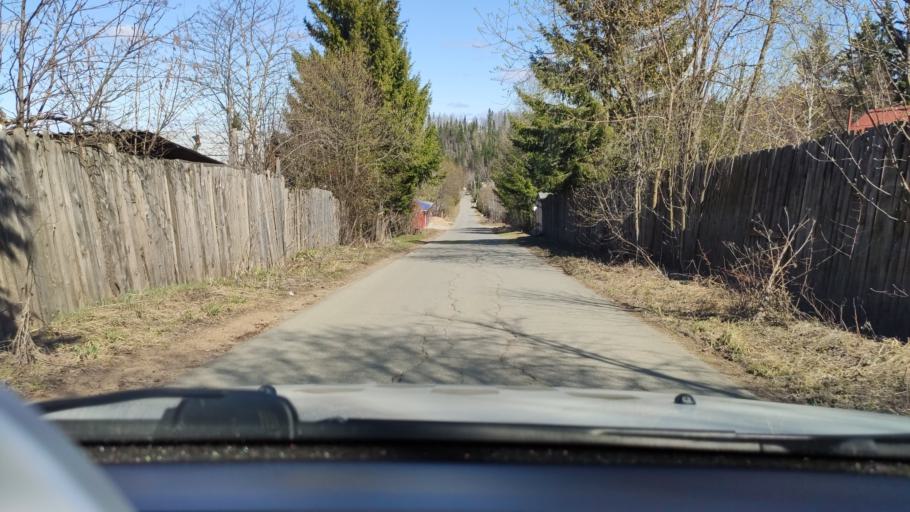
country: RU
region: Perm
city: Novyye Lyady
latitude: 58.0498
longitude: 56.6465
